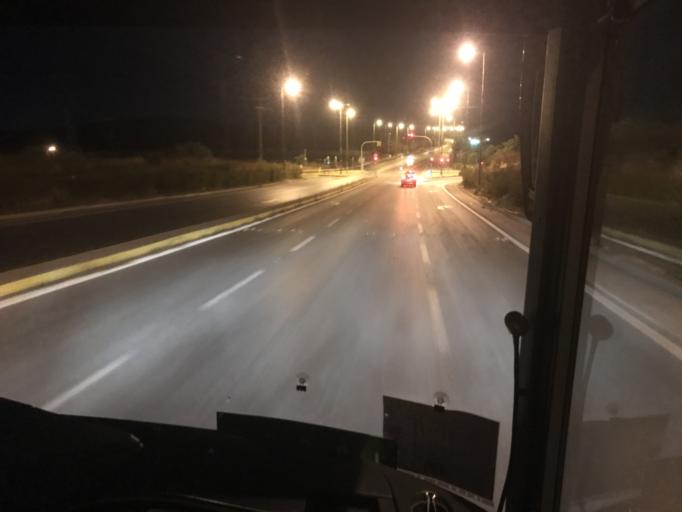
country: GR
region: Crete
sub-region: Nomos Irakleiou
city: Skalanion
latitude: 35.2817
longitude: 25.1802
